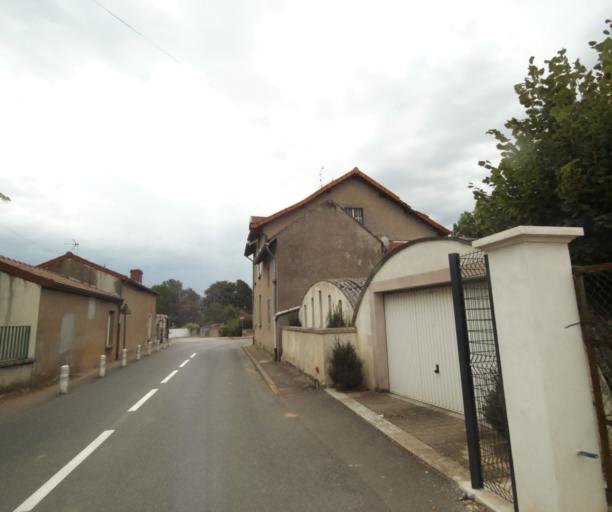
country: FR
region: Bourgogne
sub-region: Departement de Saone-et-Loire
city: Tournus
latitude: 46.5670
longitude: 4.9024
